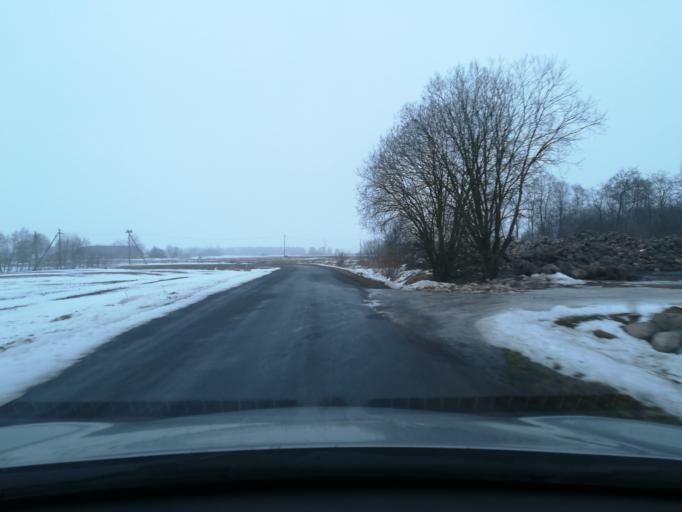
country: EE
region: Harju
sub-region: Raasiku vald
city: Raasiku
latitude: 59.3540
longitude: 25.2066
